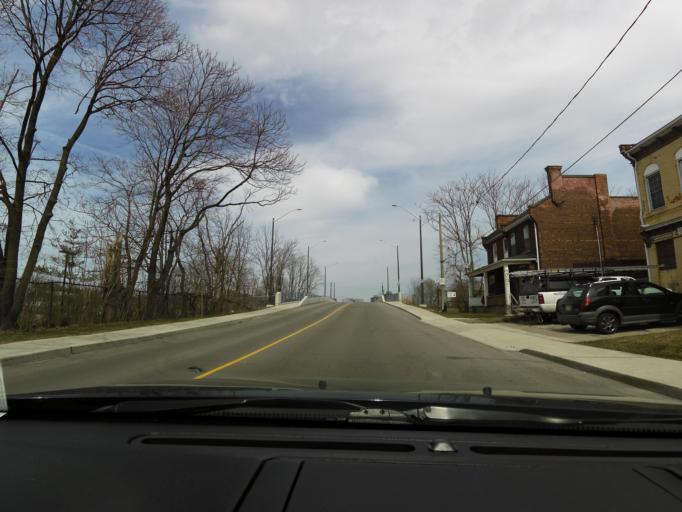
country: CA
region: Ontario
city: Hamilton
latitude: 43.2651
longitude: -79.8625
